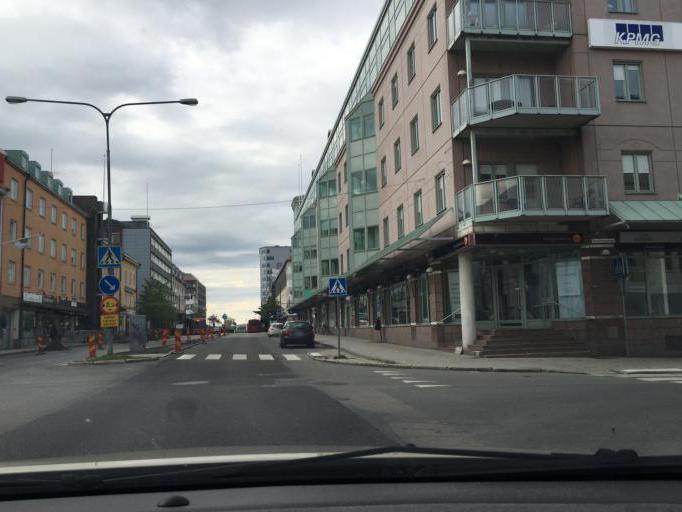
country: SE
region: Norrbotten
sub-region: Lulea Kommun
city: Lulea
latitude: 65.5827
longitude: 22.1532
